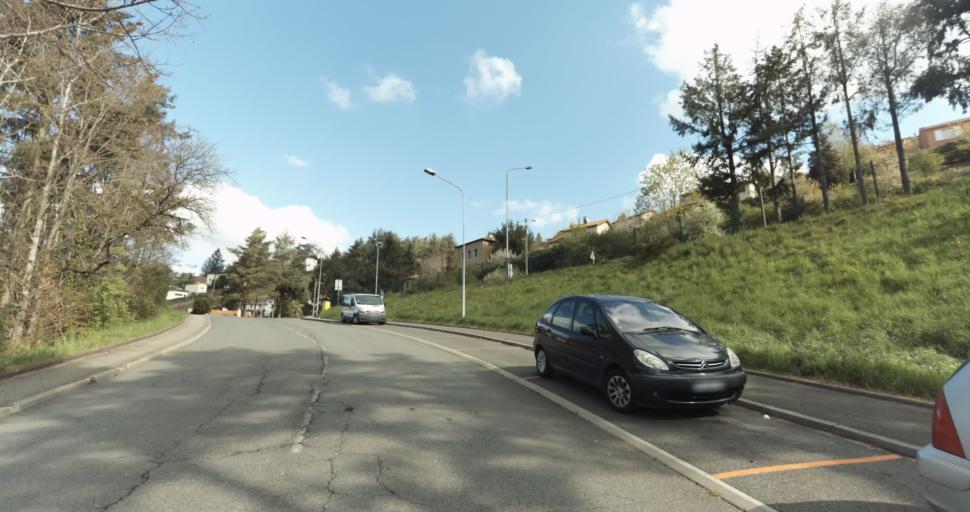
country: FR
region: Rhone-Alpes
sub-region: Departement du Rhone
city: Tarare
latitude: 45.8967
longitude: 4.4441
